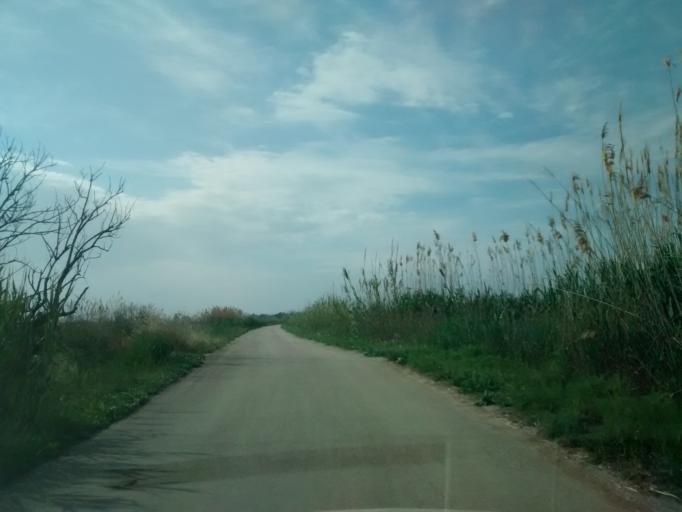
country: ES
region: Catalonia
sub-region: Provincia de Tarragona
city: Deltebre
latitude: 40.6899
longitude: 0.8453
